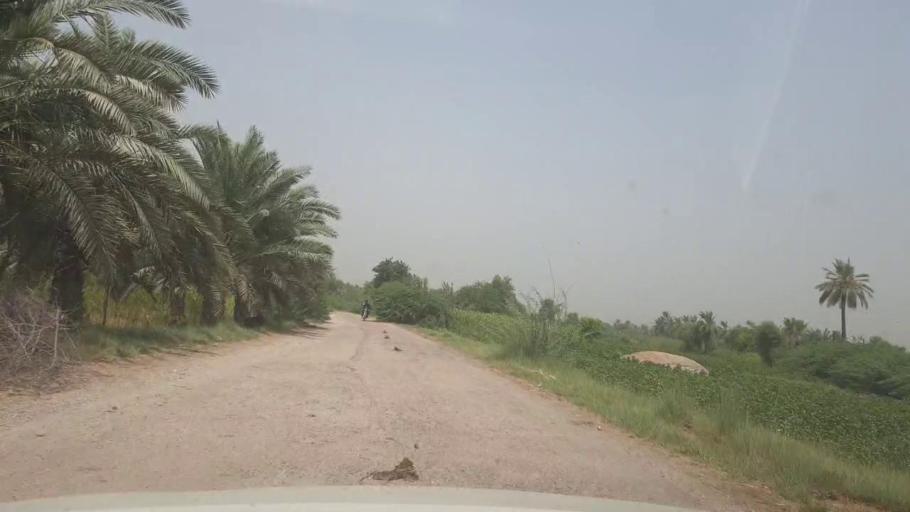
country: PK
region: Sindh
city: Kot Diji
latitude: 27.3652
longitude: 68.6575
